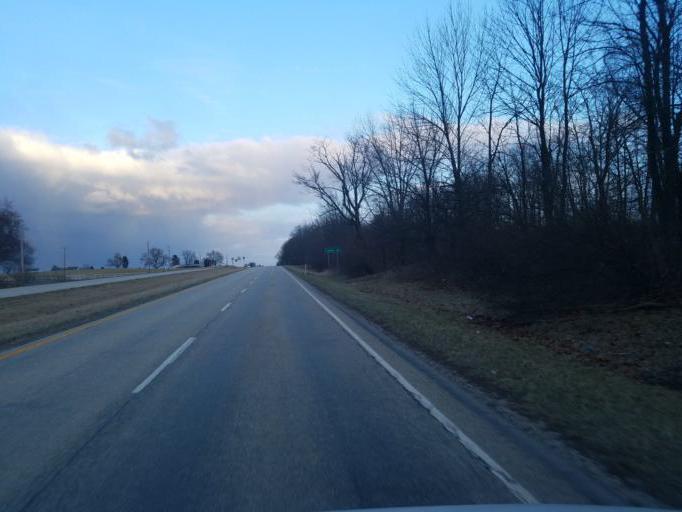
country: US
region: Indiana
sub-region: Henry County
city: Knightstown
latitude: 39.8021
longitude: -85.4723
